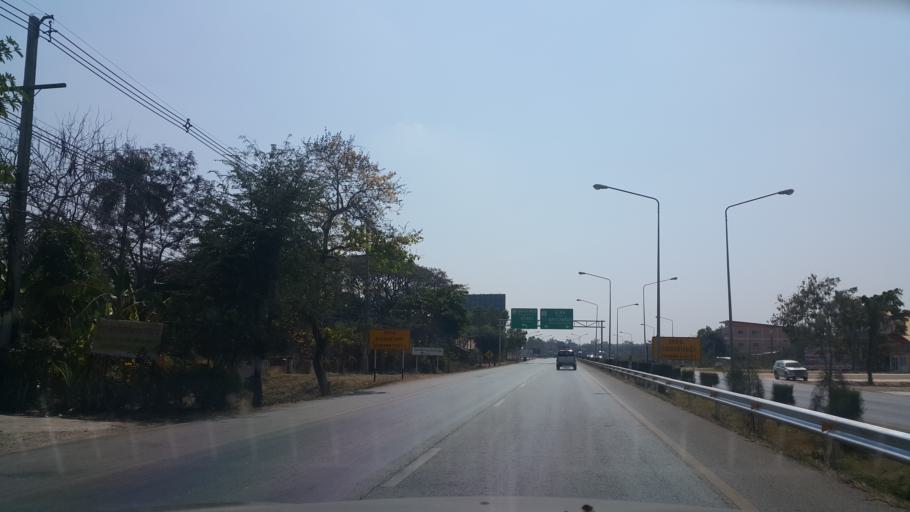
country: TH
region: Khon Kaen
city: Ban Phai
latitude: 16.0453
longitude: 102.7148
